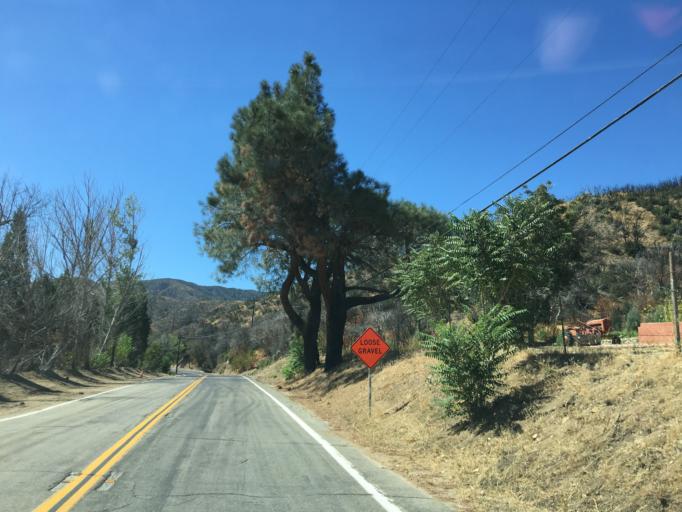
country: US
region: California
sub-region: Los Angeles County
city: Green Valley
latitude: 34.6727
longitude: -118.4554
